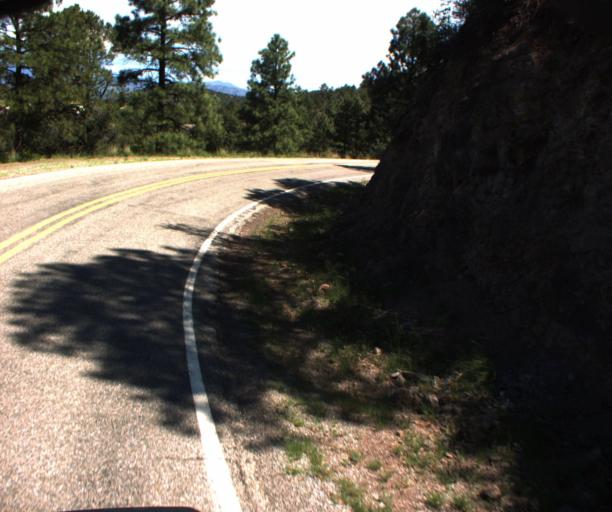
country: US
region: Arizona
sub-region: Greenlee County
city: Morenci
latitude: 33.2395
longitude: -109.3781
